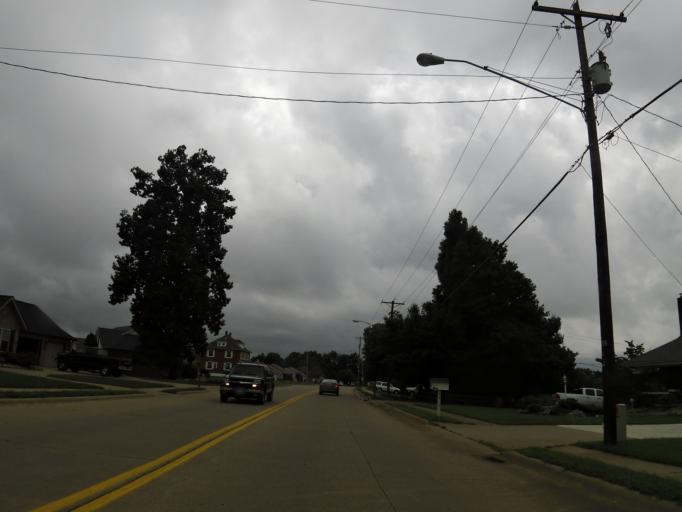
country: US
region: Missouri
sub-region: Cape Girardeau County
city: Cape Girardeau
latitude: 37.3437
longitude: -89.5571
